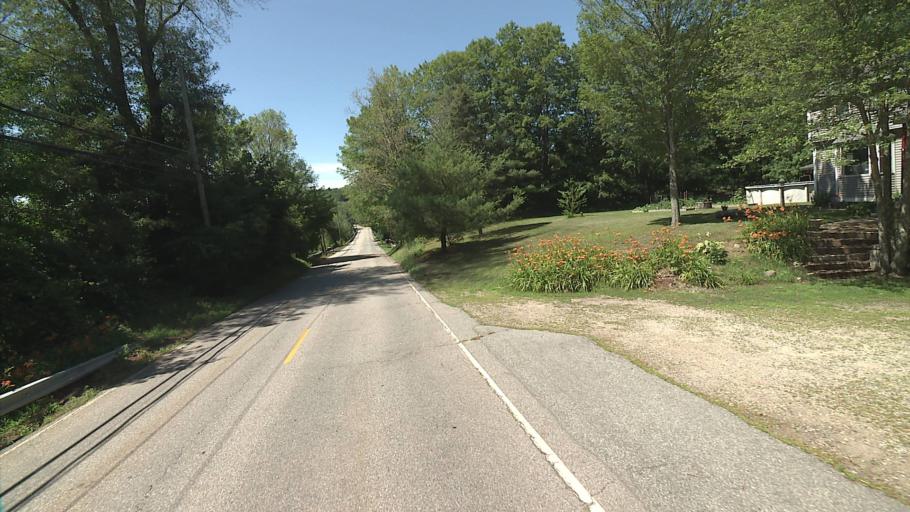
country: US
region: Connecticut
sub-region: New London County
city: Colchester
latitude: 41.6034
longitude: -72.2793
